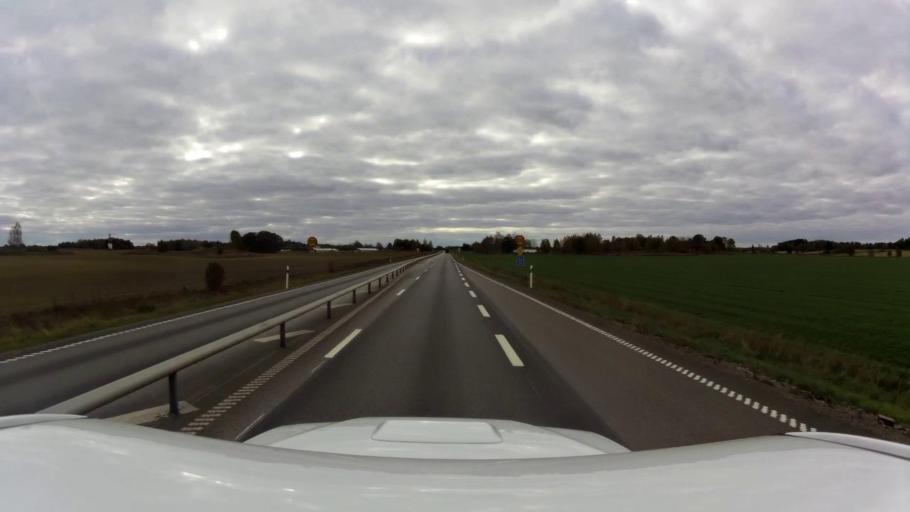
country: SE
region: OEstergoetland
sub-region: Linkopings Kommun
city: Malmslatt
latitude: 58.3500
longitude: 15.5494
